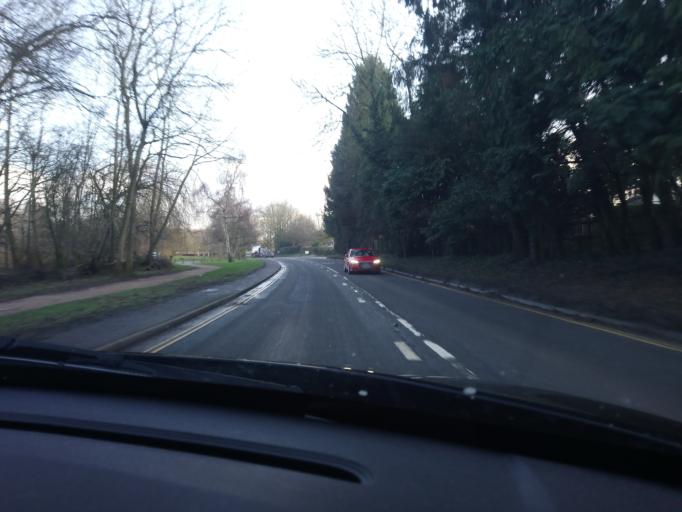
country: GB
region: England
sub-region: Shropshire
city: Ellesmere
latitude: 52.9042
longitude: -2.8821
